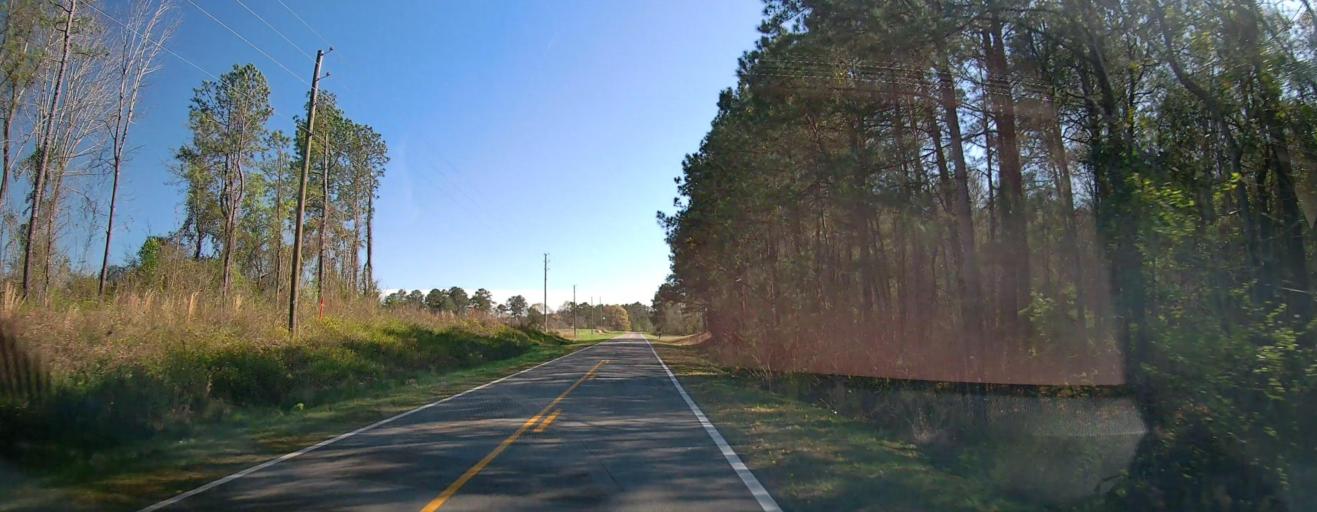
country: US
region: Georgia
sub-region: Peach County
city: Fort Valley
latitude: 32.6069
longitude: -83.9829
